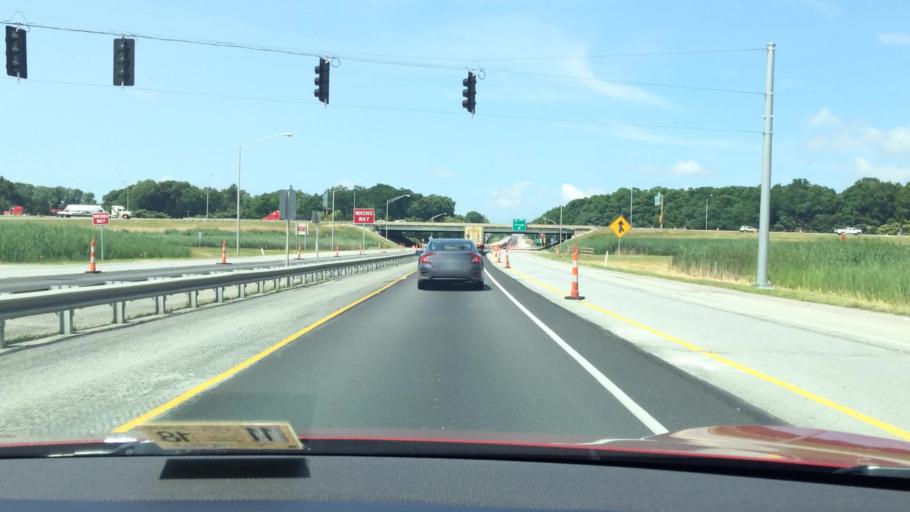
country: US
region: Indiana
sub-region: LaPorte County
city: Trail Creek
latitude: 41.6934
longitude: -86.8077
